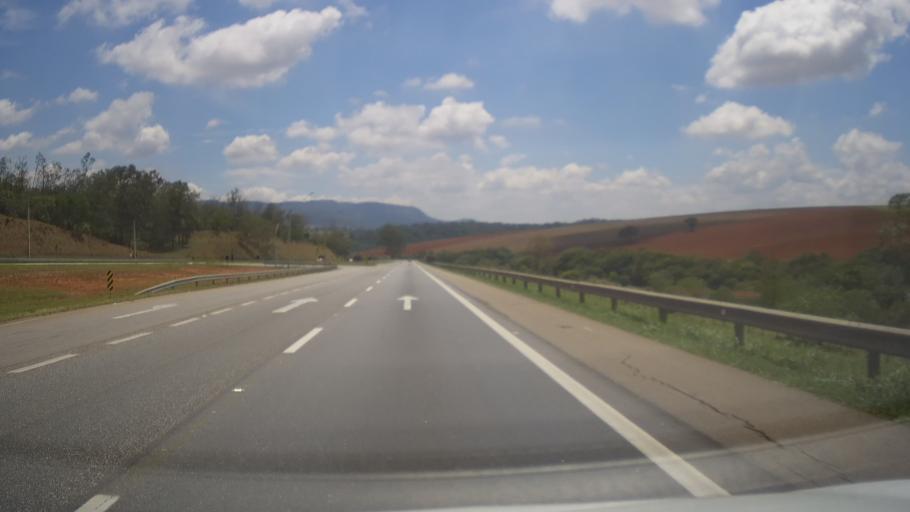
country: BR
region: Minas Gerais
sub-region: Sao Goncalo Do Sapucai
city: Sao Goncalo do Sapucai
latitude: -21.9328
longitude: -45.6127
